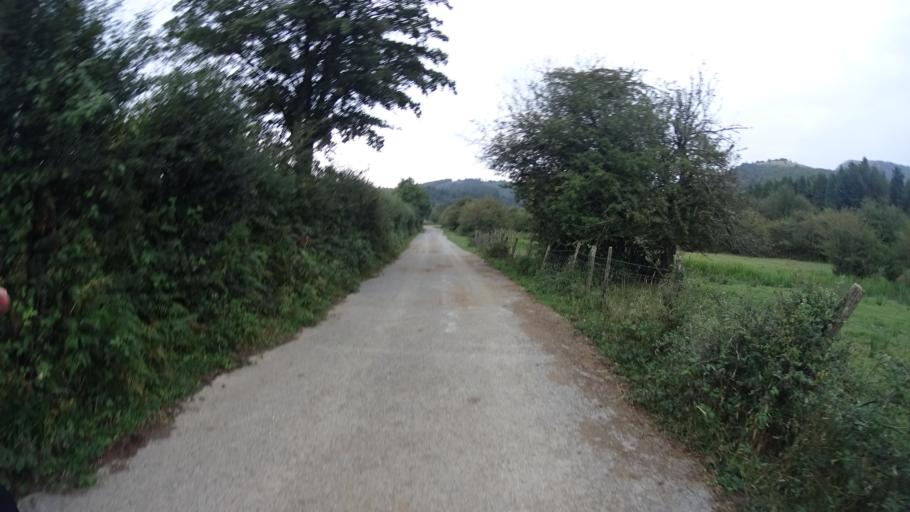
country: ES
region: Basque Country
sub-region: Bizkaia
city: Zeanuri
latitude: 43.0515
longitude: -2.7235
